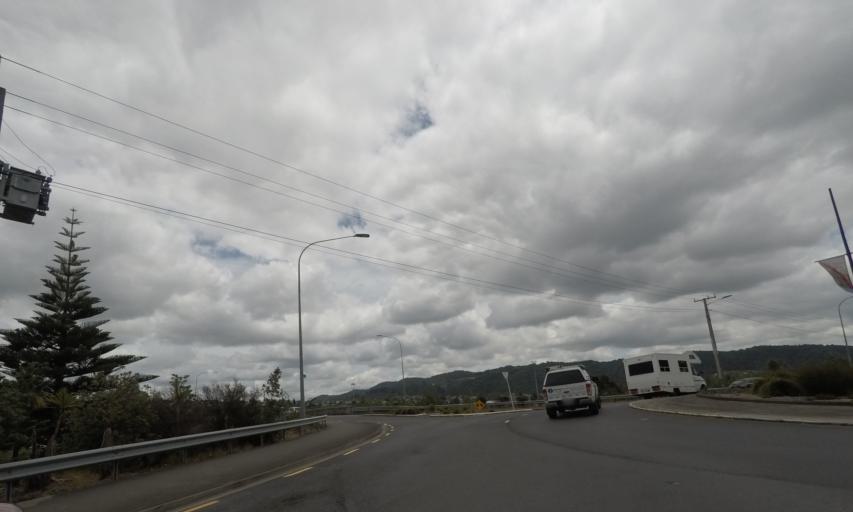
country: NZ
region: Northland
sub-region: Whangarei
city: Whangarei
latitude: -35.7336
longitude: 174.3275
